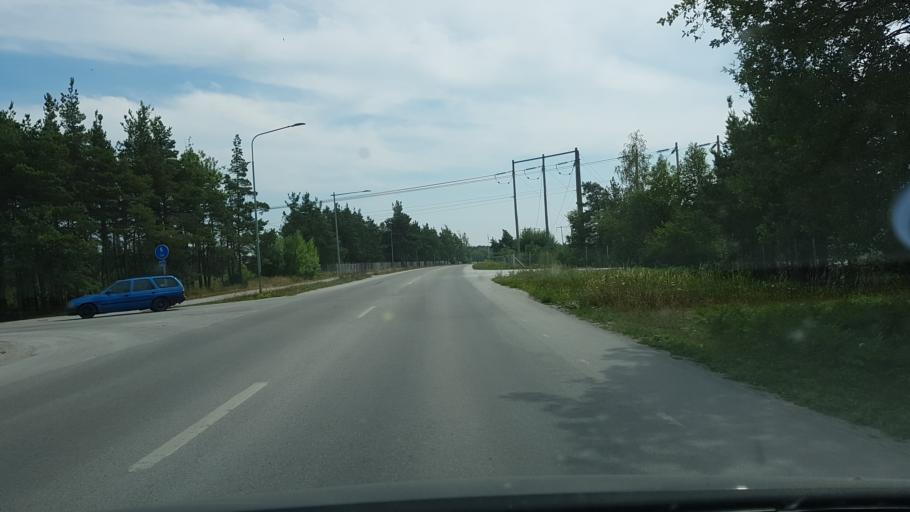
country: SE
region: Gotland
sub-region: Gotland
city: Slite
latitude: 57.7159
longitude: 18.7928
